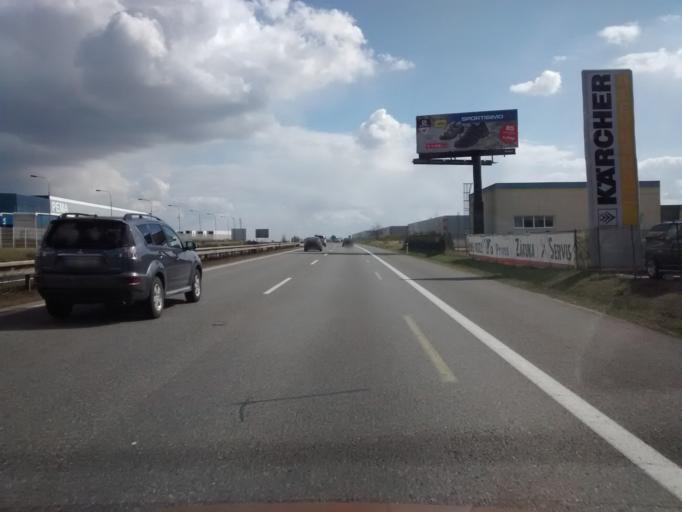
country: CZ
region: Central Bohemia
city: Zdiby
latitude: 50.1830
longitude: 14.4470
